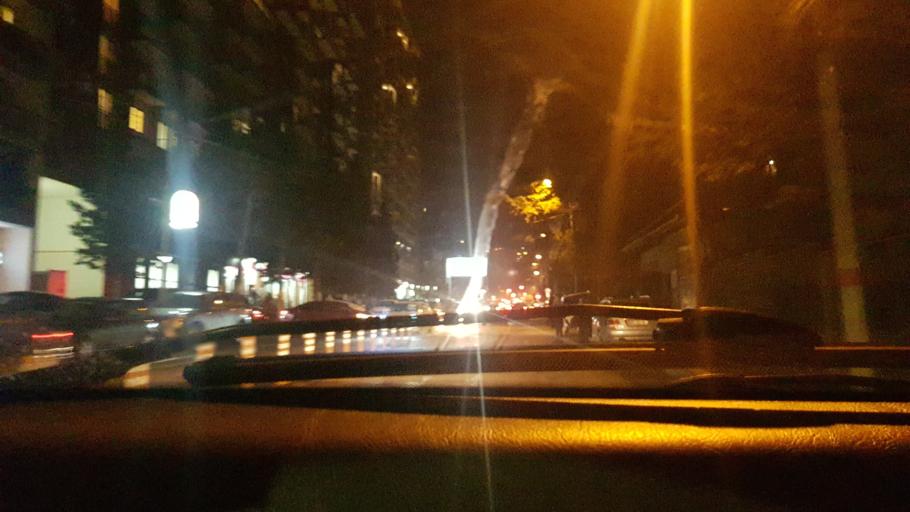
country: GE
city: Tsqnet'i
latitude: 41.7220
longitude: 44.7510
